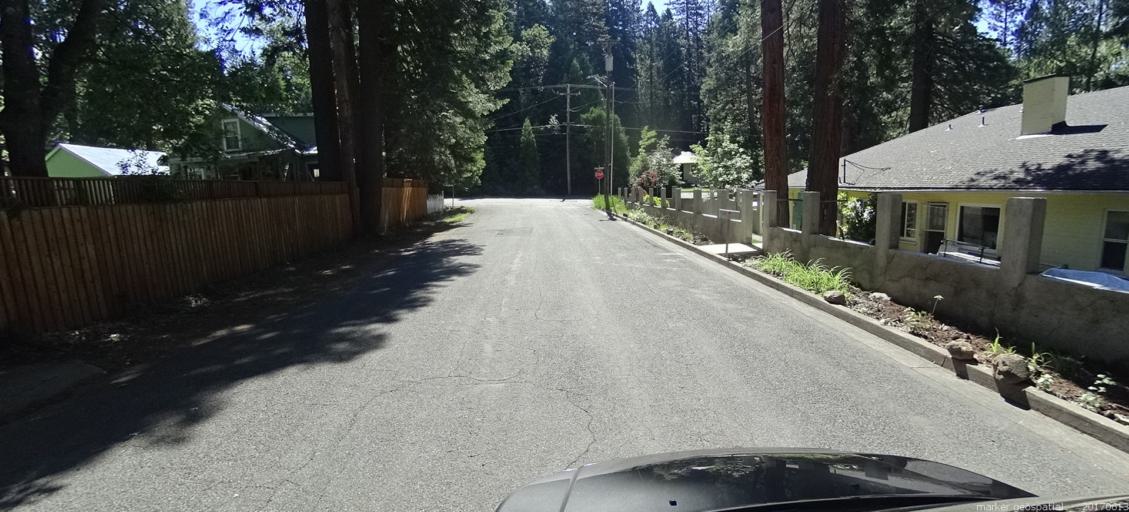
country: US
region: California
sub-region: Siskiyou County
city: Mount Shasta
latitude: 41.3095
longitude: -122.3070
